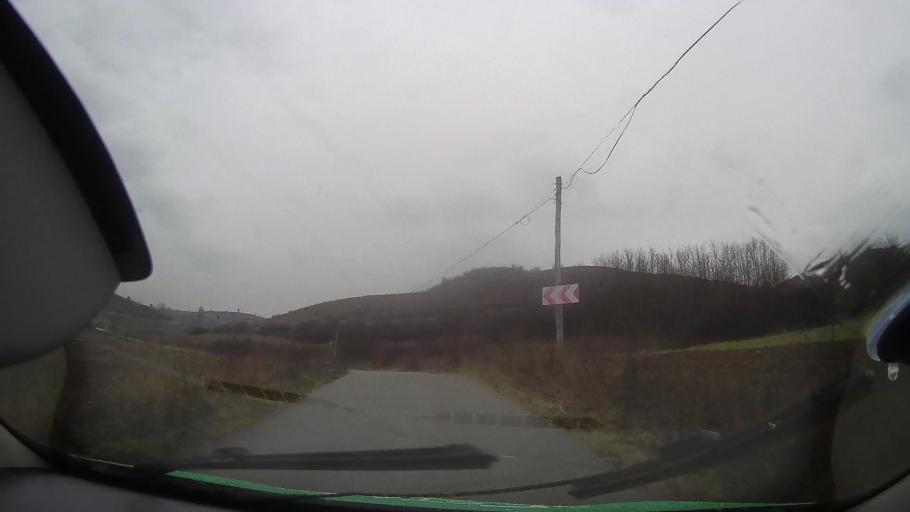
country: RO
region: Bihor
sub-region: Comuna Uileacu de Beius
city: Uileacu de Beius
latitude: 46.6935
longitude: 22.2178
